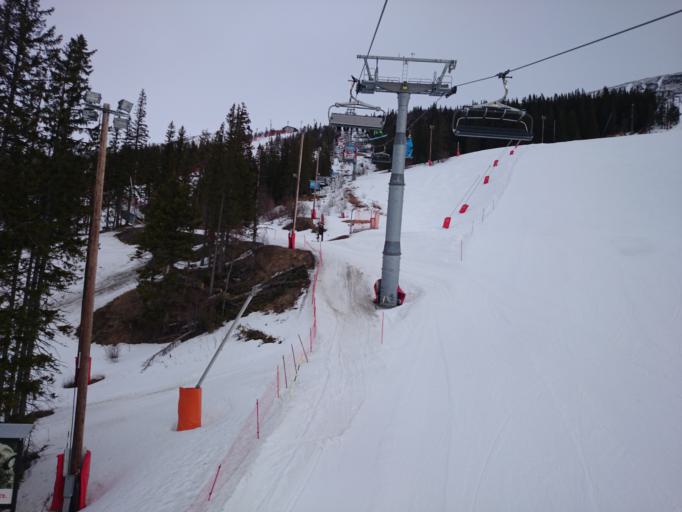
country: SE
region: Jaemtland
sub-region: Are Kommun
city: Are
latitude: 63.4095
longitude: 13.0613
